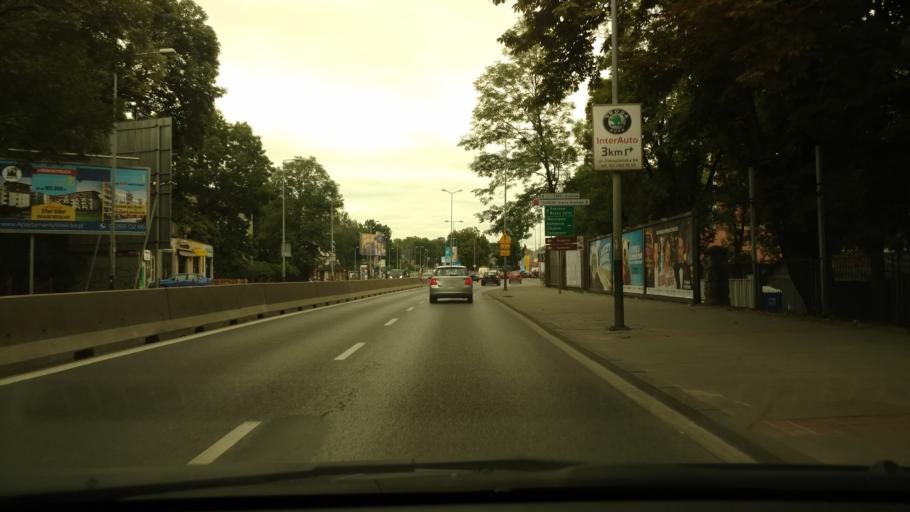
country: PL
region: Lesser Poland Voivodeship
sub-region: Krakow
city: Krakow
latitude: 50.0382
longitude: 19.9386
